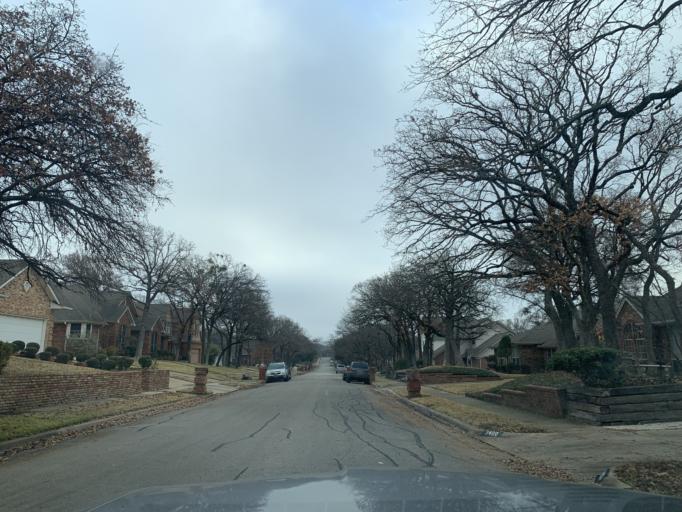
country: US
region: Texas
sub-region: Tarrant County
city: Bedford
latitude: 32.8326
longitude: -97.1476
